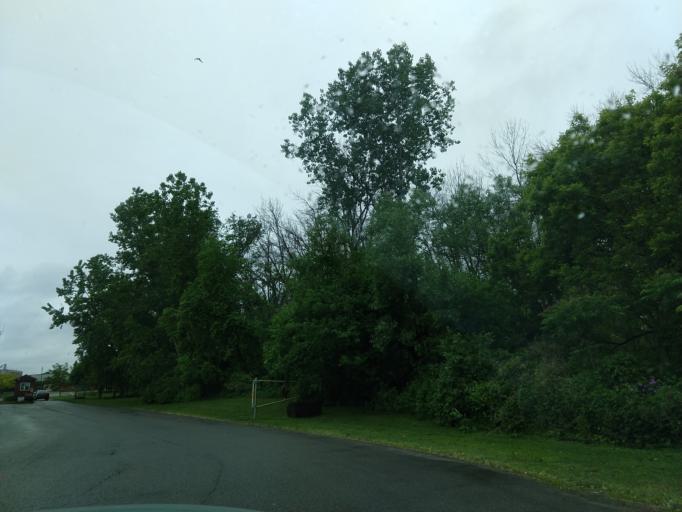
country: US
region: New York
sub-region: Erie County
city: Blasdell
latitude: 42.7901
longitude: -78.8504
